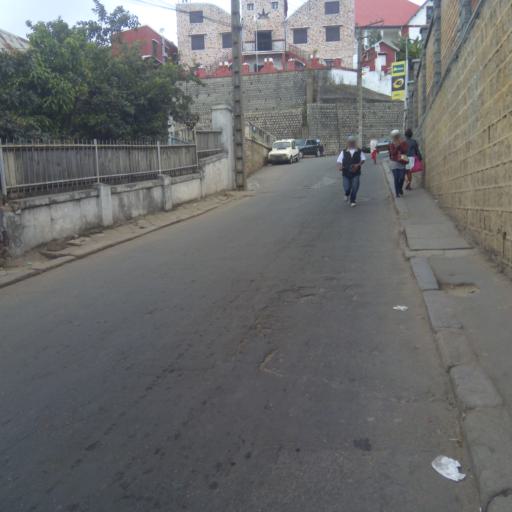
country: MG
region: Analamanga
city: Antananarivo
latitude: -18.9200
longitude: 47.5320
